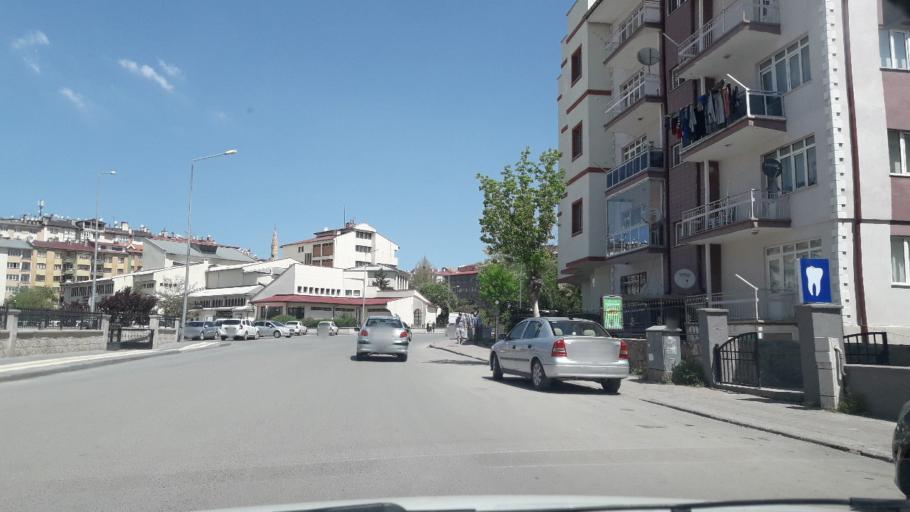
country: TR
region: Sivas
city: Sivas
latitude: 39.7423
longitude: 37.0121
